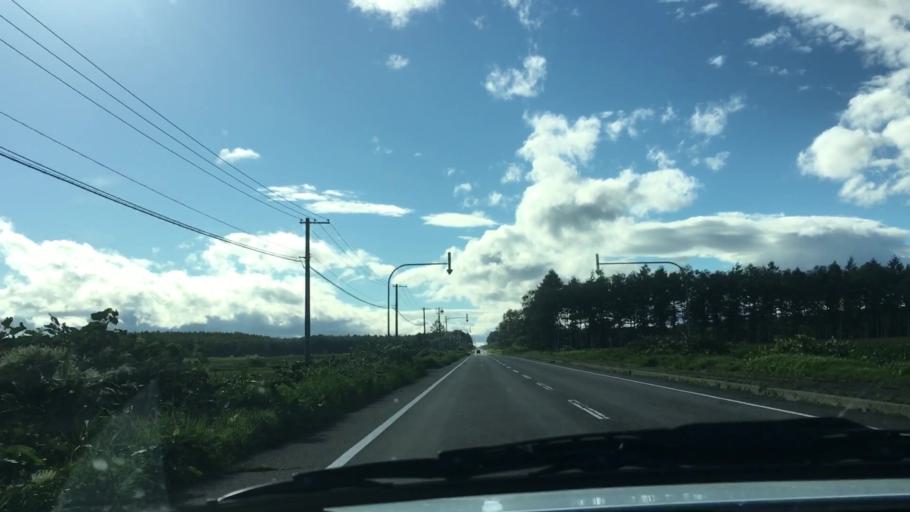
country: JP
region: Hokkaido
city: Otofuke
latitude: 43.1613
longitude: 143.1596
